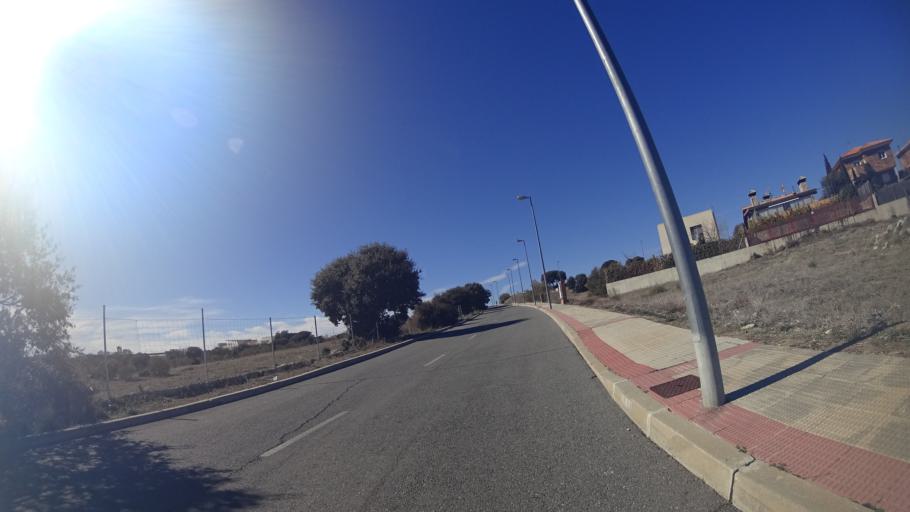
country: ES
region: Madrid
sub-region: Provincia de Madrid
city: Colmenarejo
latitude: 40.5475
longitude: -4.0085
